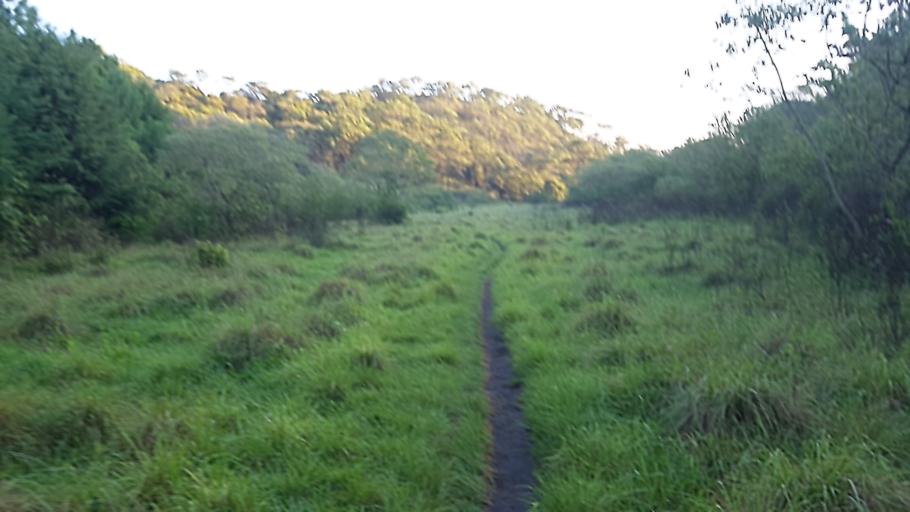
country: MX
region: Nayarit
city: Tepic
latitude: 21.5001
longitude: -104.9306
